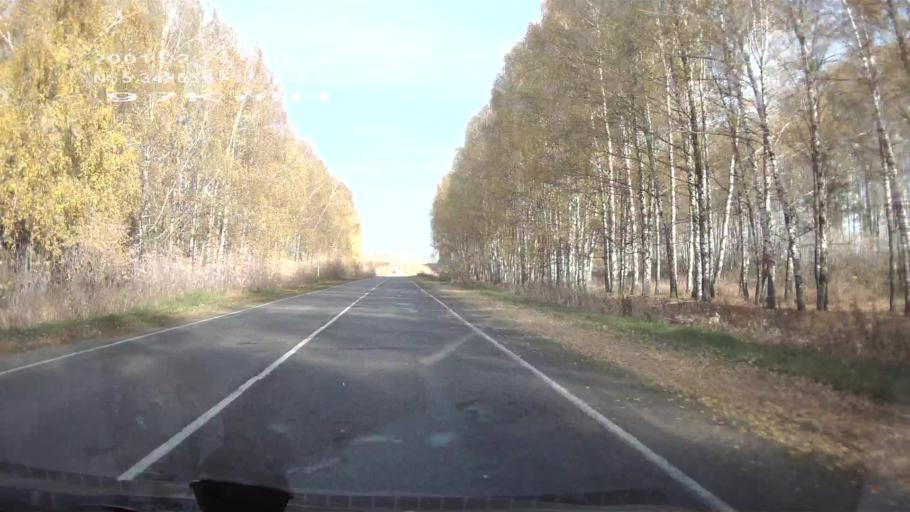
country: RU
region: Chuvashia
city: Ibresi
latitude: 55.3487
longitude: 47.1859
